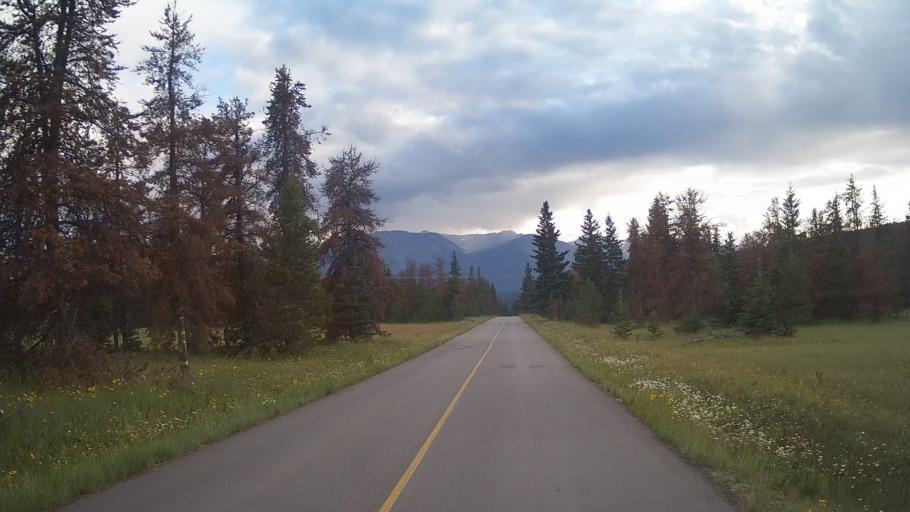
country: CA
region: Alberta
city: Jasper Park Lodge
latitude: 52.9284
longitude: -118.0297
